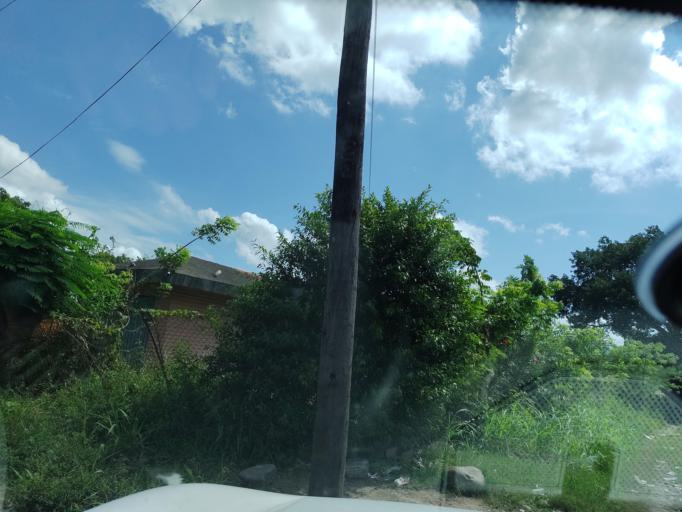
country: MX
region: Veracruz
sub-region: Martinez de la Torre
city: El Progreso
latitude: 20.1136
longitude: -97.0116
